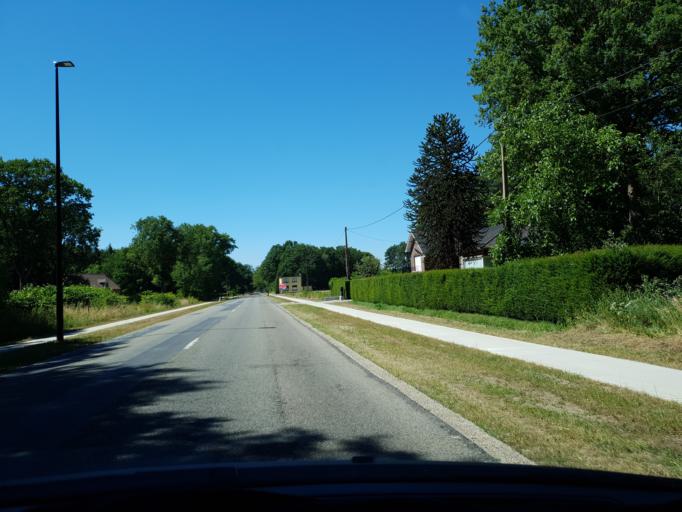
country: BE
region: Flanders
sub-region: Provincie Antwerpen
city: Olen
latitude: 51.1641
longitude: 4.8694
